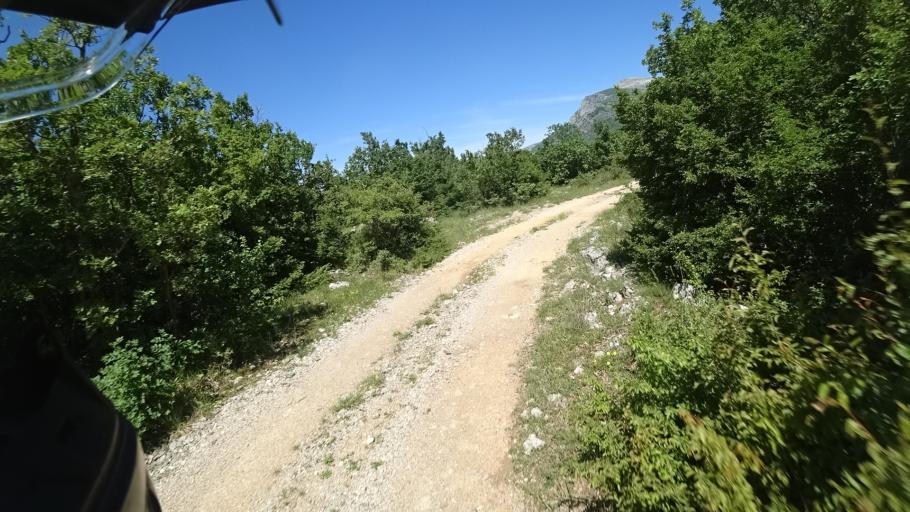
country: BA
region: Federation of Bosnia and Herzegovina
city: Bosansko Grahovo
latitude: 43.9915
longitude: 16.4186
